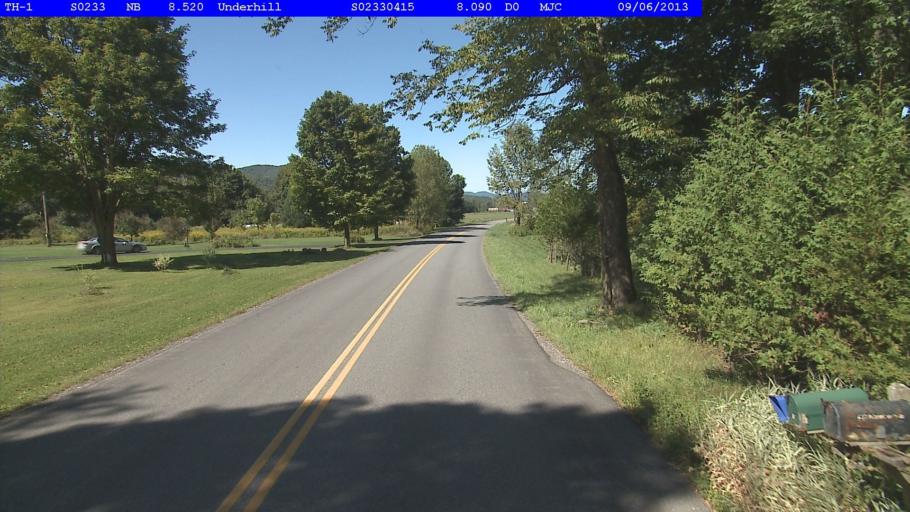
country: US
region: Vermont
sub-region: Chittenden County
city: Jericho
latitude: 44.5812
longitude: -72.8631
